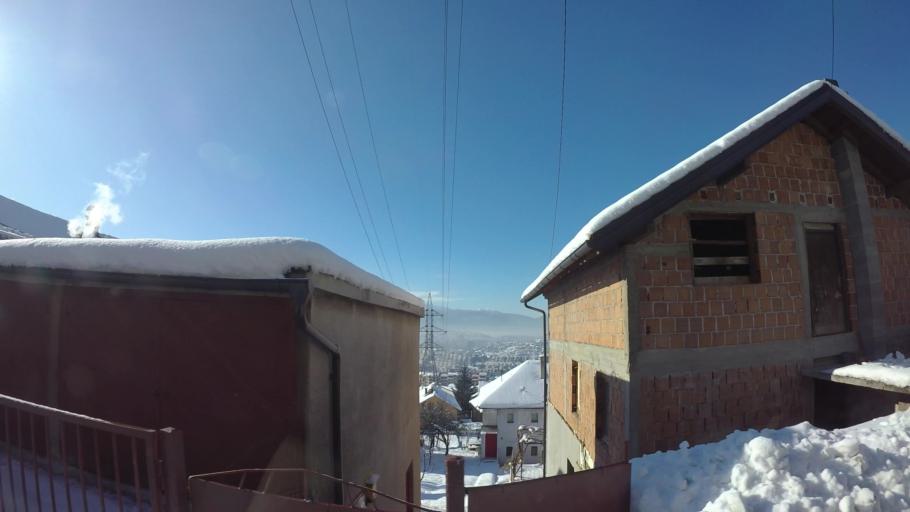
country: BA
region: Federation of Bosnia and Herzegovina
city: Kobilja Glava
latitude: 43.8745
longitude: 18.4226
